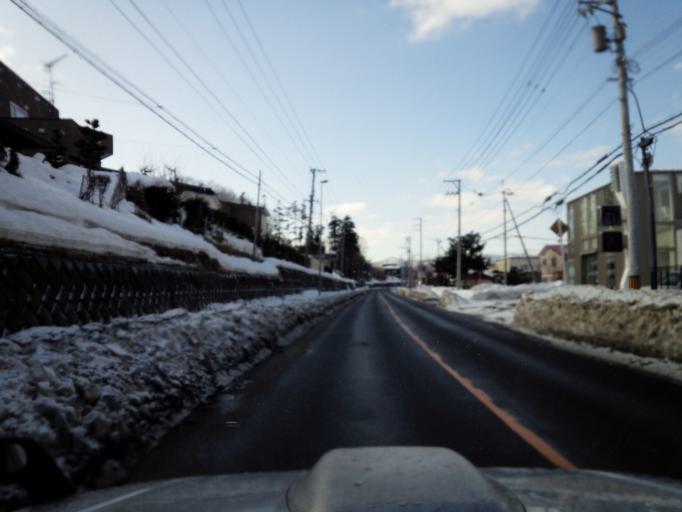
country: JP
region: Hokkaido
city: Sapporo
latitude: 42.9459
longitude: 141.3468
